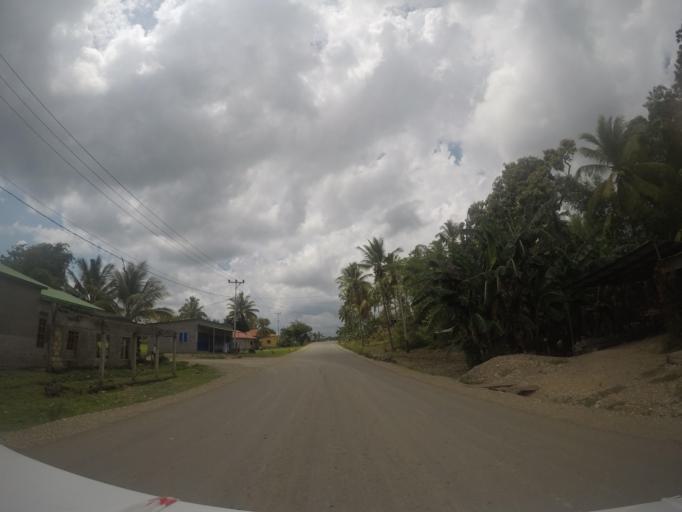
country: TL
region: Baucau
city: Baucau
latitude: -8.5493
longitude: 126.4108
